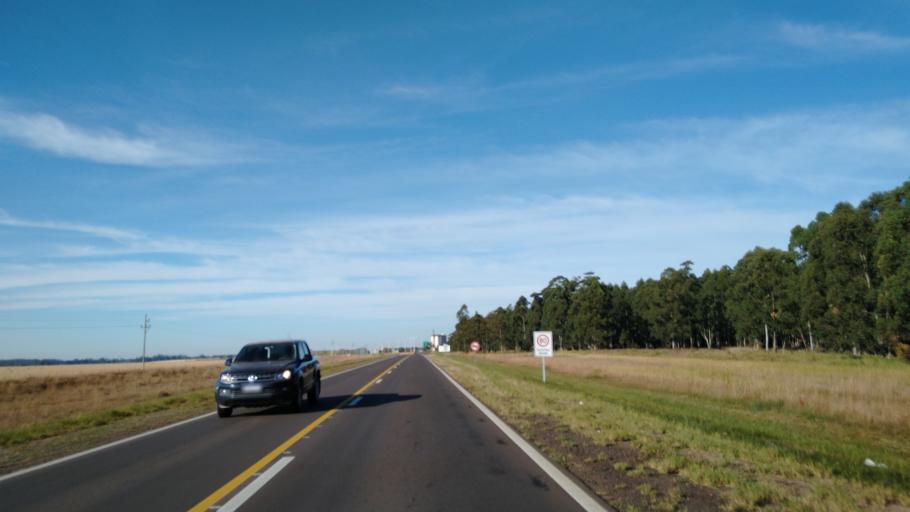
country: AR
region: Corrientes
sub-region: Departamento de Paso de los Libres
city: Paso de los Libres
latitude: -29.7021
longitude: -57.2113
